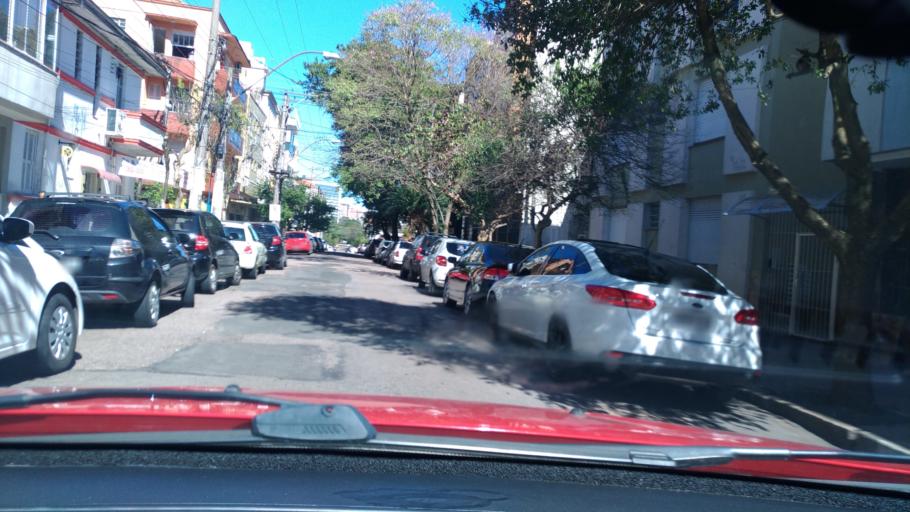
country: BR
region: Rio Grande do Sul
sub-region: Porto Alegre
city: Porto Alegre
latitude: -30.0391
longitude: -51.2093
